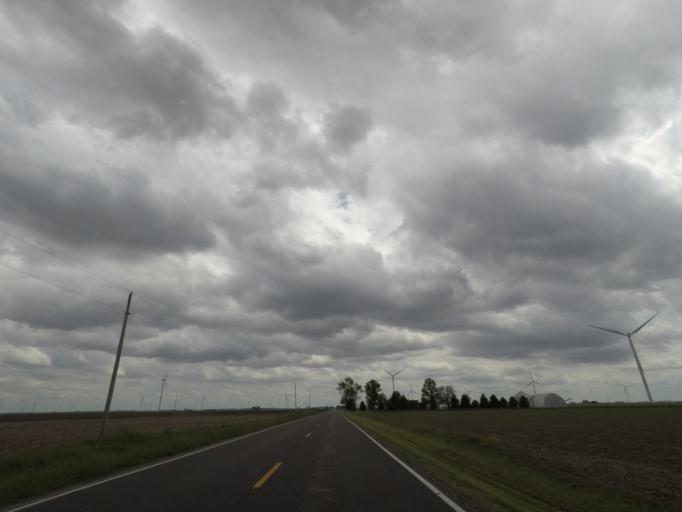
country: US
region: Illinois
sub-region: Macon County
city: Warrensburg
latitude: 40.0218
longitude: -89.0855
